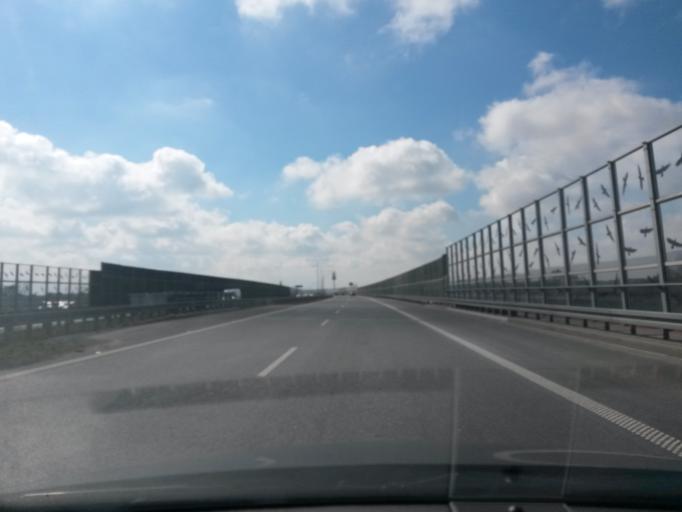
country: PL
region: Lodz Voivodeship
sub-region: powiat Lowicki
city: Bobrowniki
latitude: 52.0335
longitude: 20.0144
